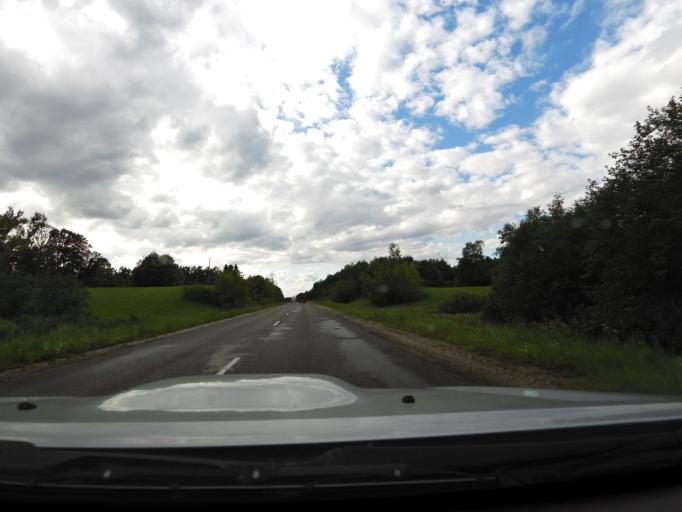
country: LV
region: Akniste
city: Akniste
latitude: 55.9960
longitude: 25.9674
